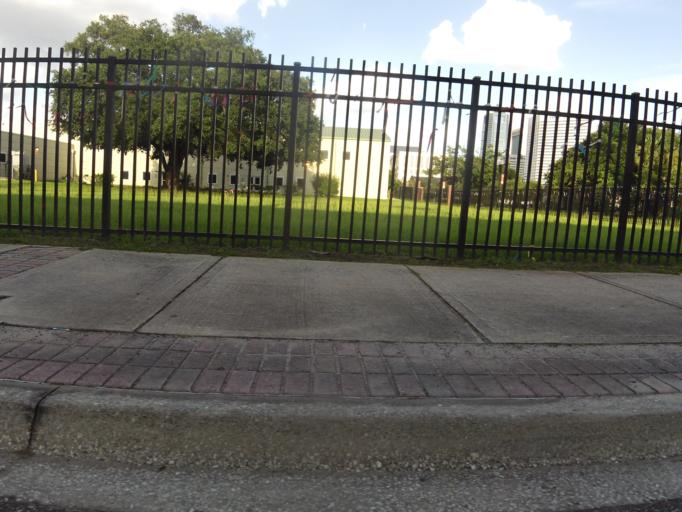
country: US
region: Florida
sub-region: Duval County
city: Jacksonville
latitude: 30.3318
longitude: -81.6681
